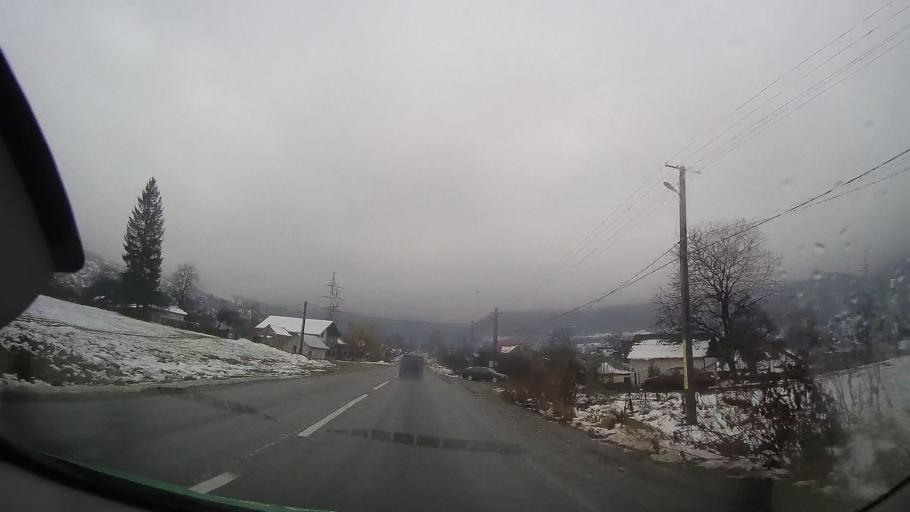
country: RO
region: Neamt
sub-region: Comuna Pangarati
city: Stejaru
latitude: 46.9098
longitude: 26.1786
